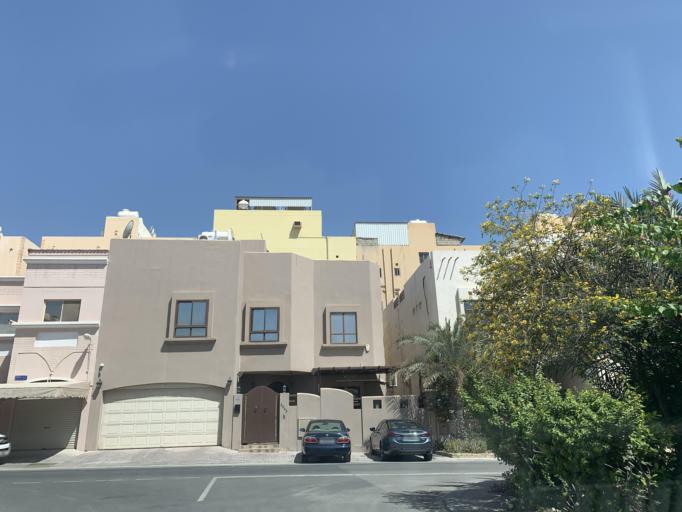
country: BH
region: Northern
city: Ar Rifa'
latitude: 26.1384
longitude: 50.5779
